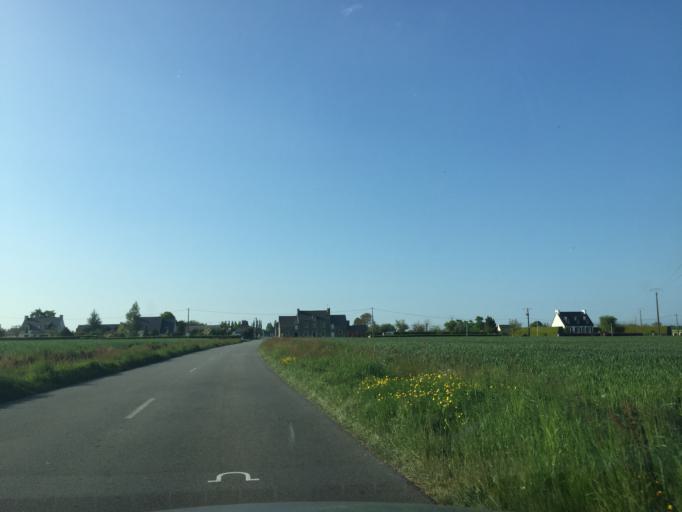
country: FR
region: Brittany
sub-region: Departement des Cotes-d'Armor
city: Crehen
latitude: 48.5571
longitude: -2.2400
